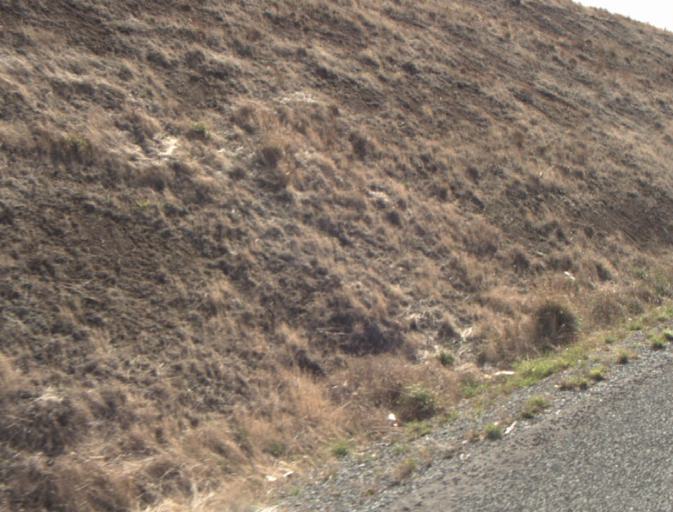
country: AU
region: Tasmania
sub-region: Launceston
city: Mayfield
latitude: -41.3559
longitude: 147.1048
